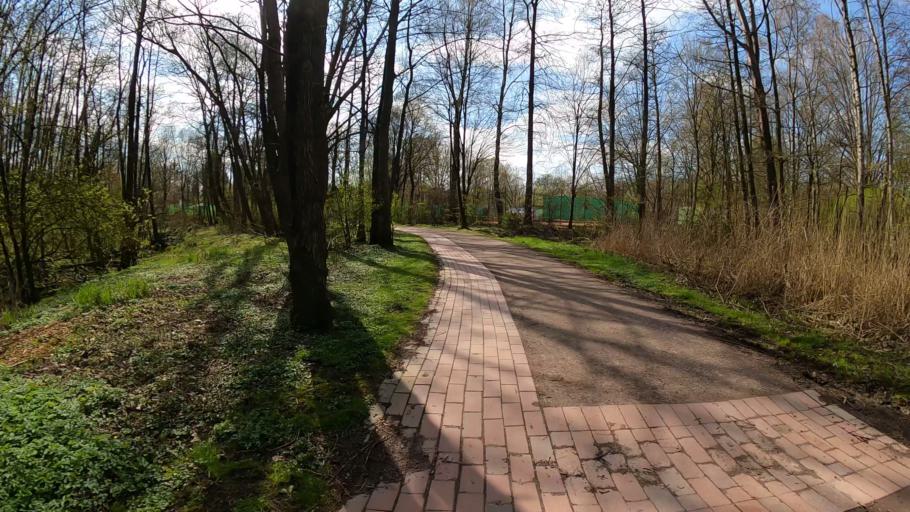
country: DE
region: Hamburg
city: Harburg
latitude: 53.4375
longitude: 9.9774
